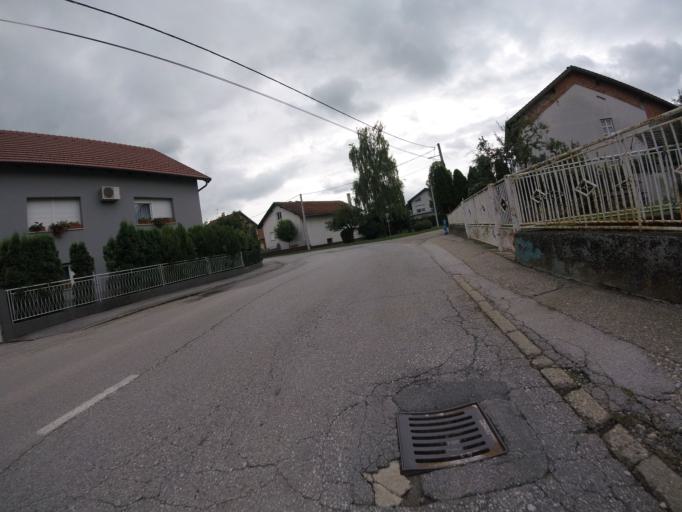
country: HR
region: Zagrebacka
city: Gradici
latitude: 45.7043
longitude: 16.0372
